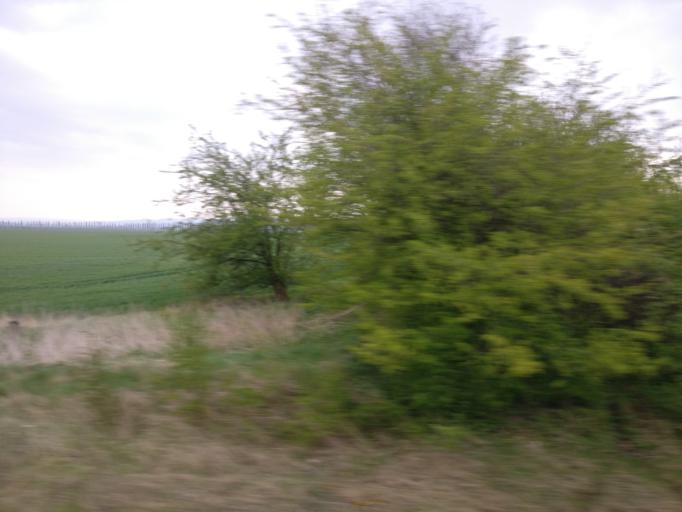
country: DE
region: Saxony-Anhalt
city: Heudeber
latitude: 51.9045
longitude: 10.8705
